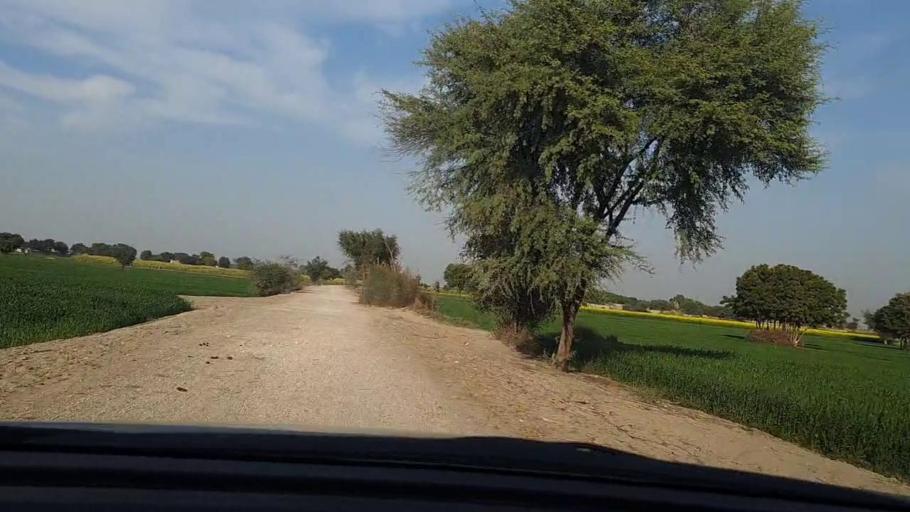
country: PK
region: Sindh
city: Daulatpur
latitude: 26.3286
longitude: 68.0268
